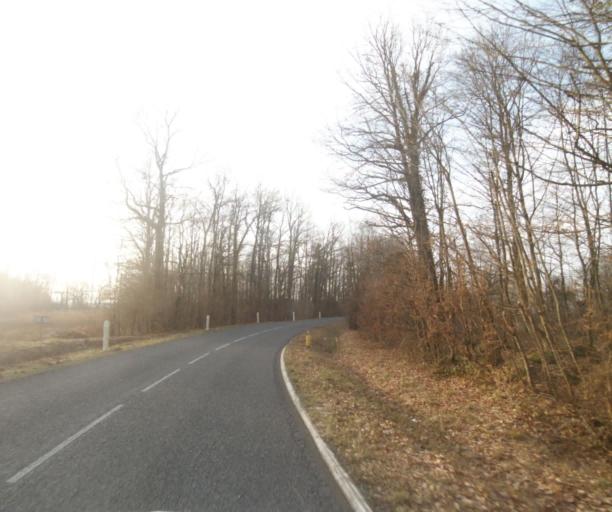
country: FR
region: Champagne-Ardenne
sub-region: Departement de la Haute-Marne
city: Bettancourt-la-Ferree
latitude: 48.6620
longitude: 4.9448
